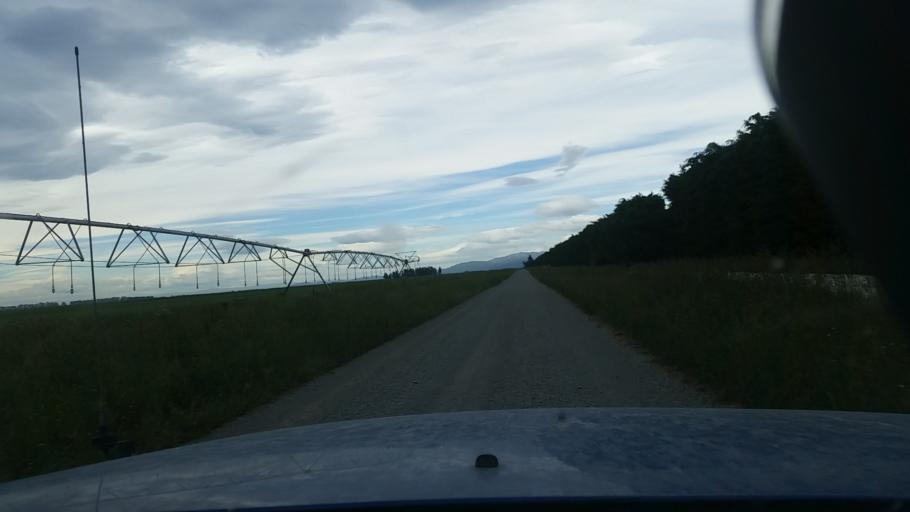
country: NZ
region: Canterbury
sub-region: Ashburton District
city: Methven
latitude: -43.7893
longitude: 171.5256
